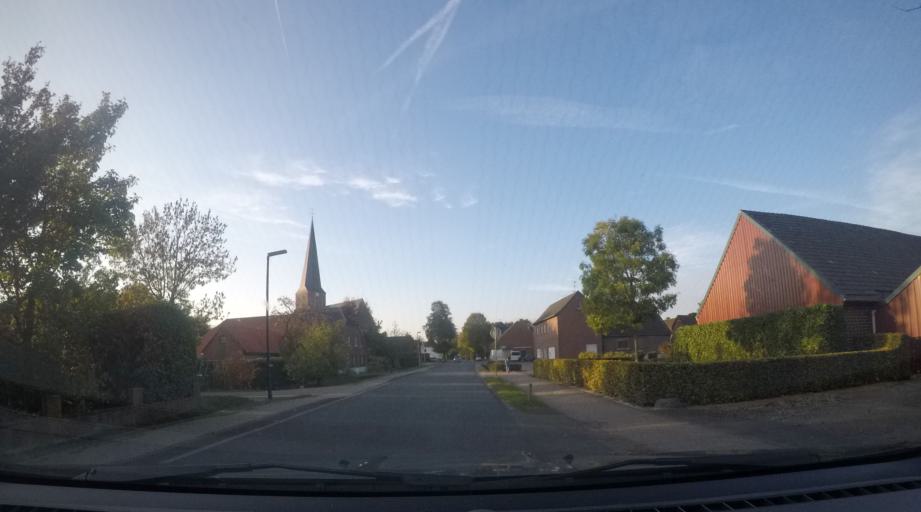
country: DE
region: North Rhine-Westphalia
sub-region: Regierungsbezirk Dusseldorf
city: Mehrhoog
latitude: 51.7914
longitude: 6.5258
